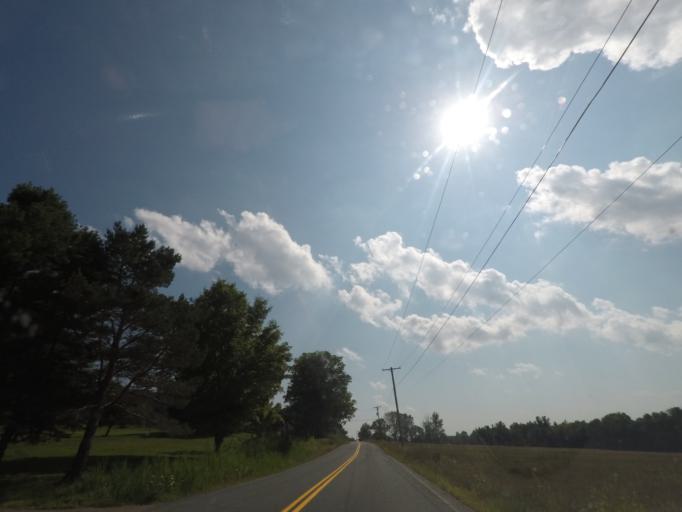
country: US
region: New York
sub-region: Rensselaer County
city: Averill Park
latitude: 42.6510
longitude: -73.5252
